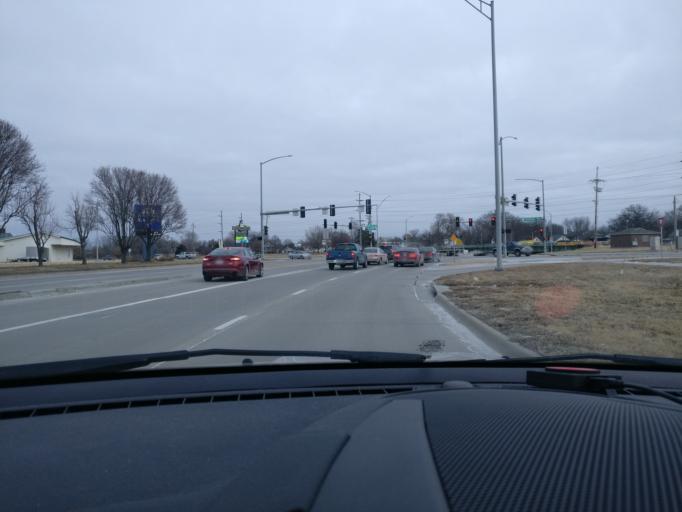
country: US
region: Nebraska
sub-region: Lancaster County
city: Lincoln
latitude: 40.8579
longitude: -96.6441
